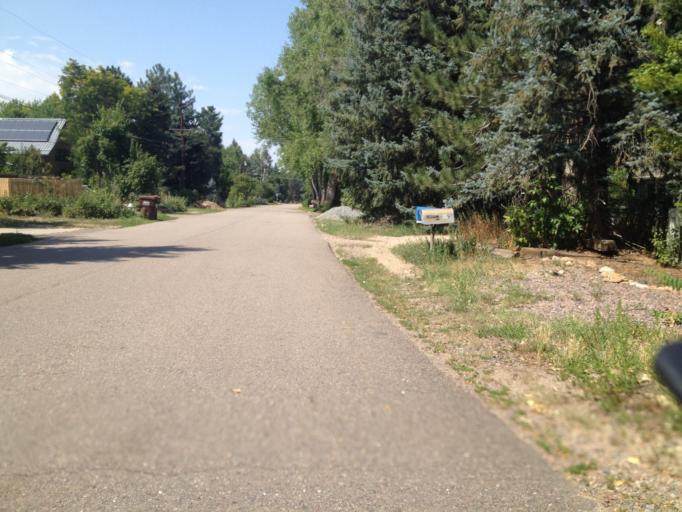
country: US
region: Colorado
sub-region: Boulder County
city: Boulder
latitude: 40.0020
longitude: -105.2145
